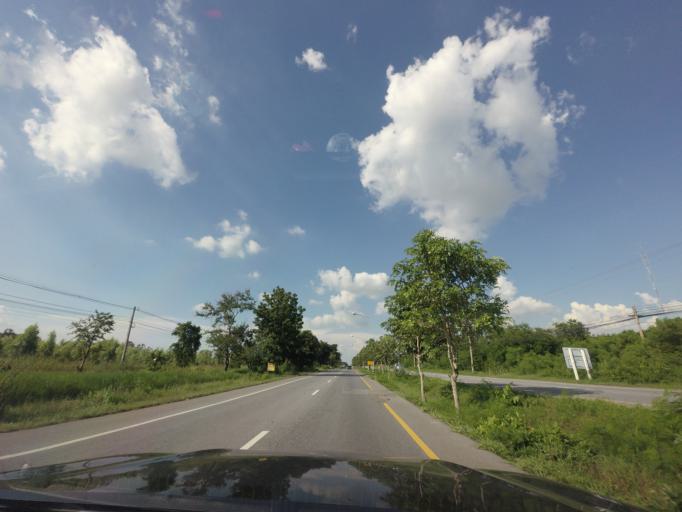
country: TH
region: Khon Kaen
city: Phon
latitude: 15.7287
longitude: 102.5946
